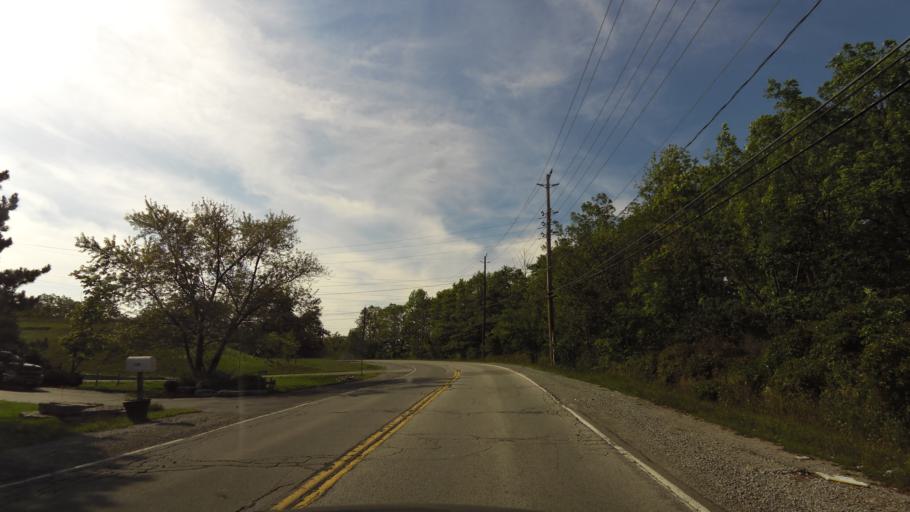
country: CA
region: Ontario
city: Hamilton
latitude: 43.3154
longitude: -79.8647
